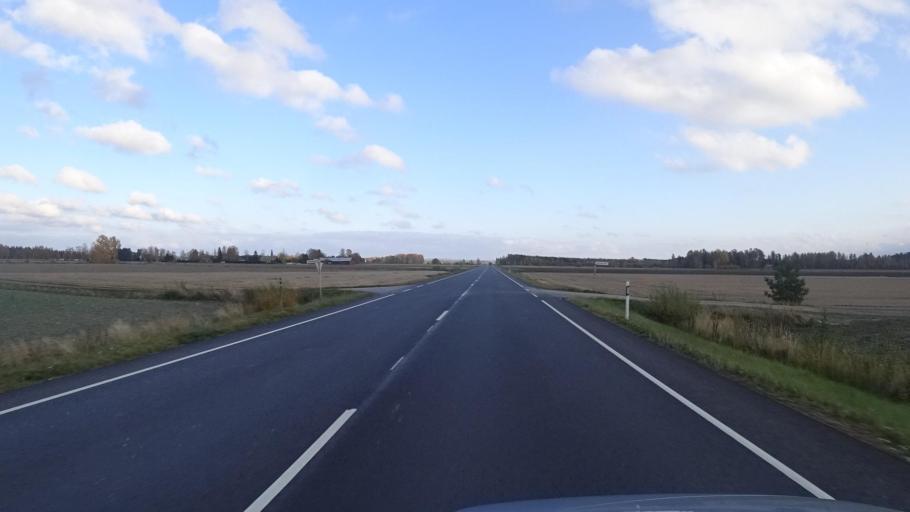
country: FI
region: Satakunta
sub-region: Rauma
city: Koeylioe
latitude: 61.0772
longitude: 22.2861
